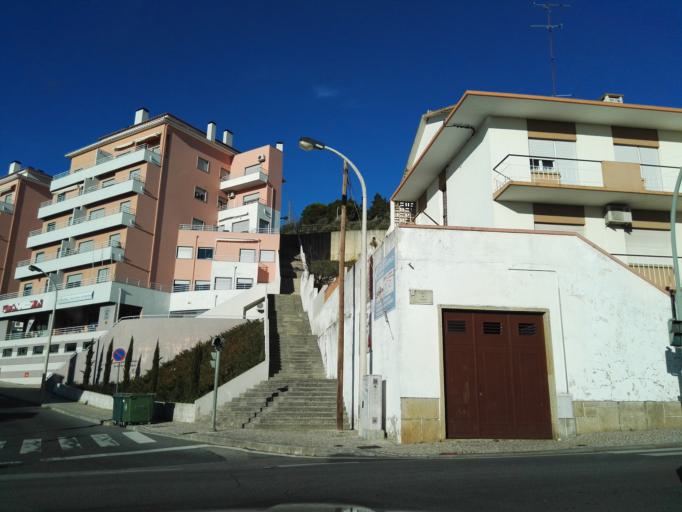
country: PT
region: Castelo Branco
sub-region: Castelo Branco
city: Castelo Branco
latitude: 39.8234
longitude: -7.4984
